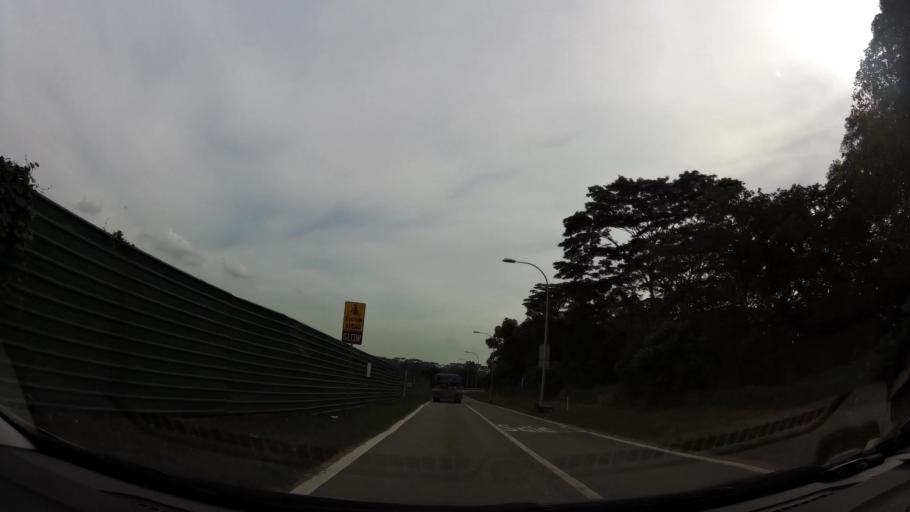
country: MY
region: Johor
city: Johor Bahru
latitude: 1.4258
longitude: 103.7208
